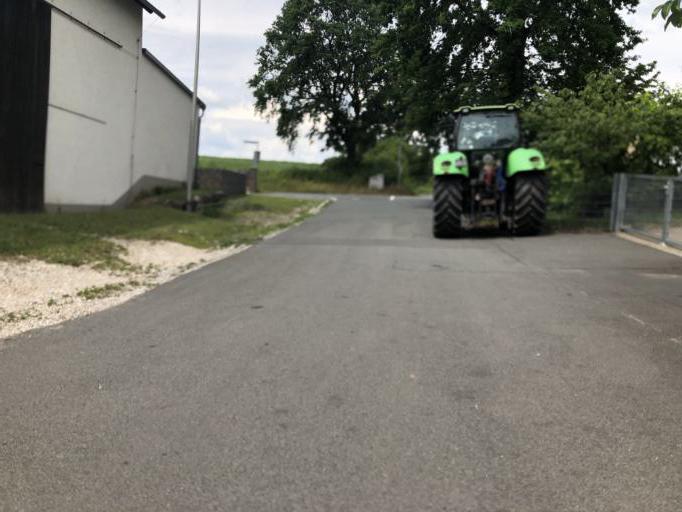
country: DE
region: Bavaria
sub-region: Regierungsbezirk Mittelfranken
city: Obermichelbach
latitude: 49.5631
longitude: 10.9266
